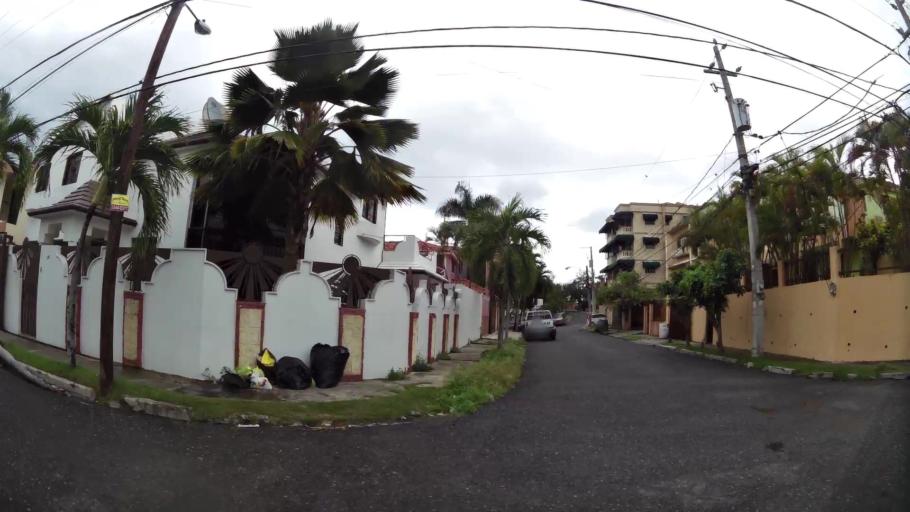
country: DO
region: Nacional
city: La Agustina
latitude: 18.5041
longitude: -69.9384
